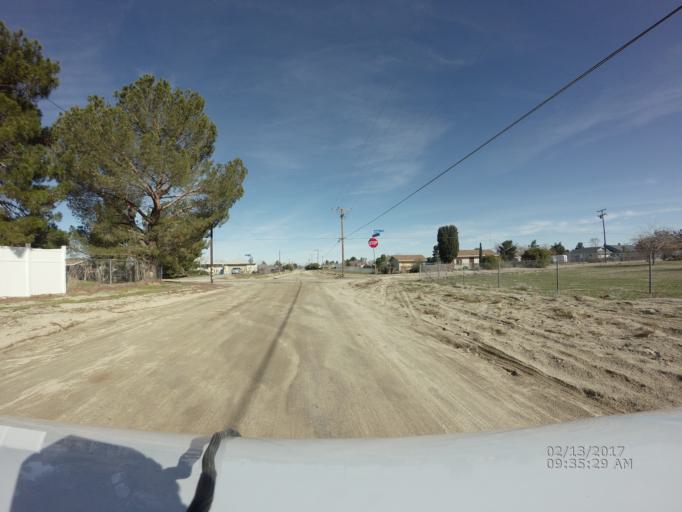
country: US
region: California
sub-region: Los Angeles County
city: Littlerock
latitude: 34.5318
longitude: -117.9669
